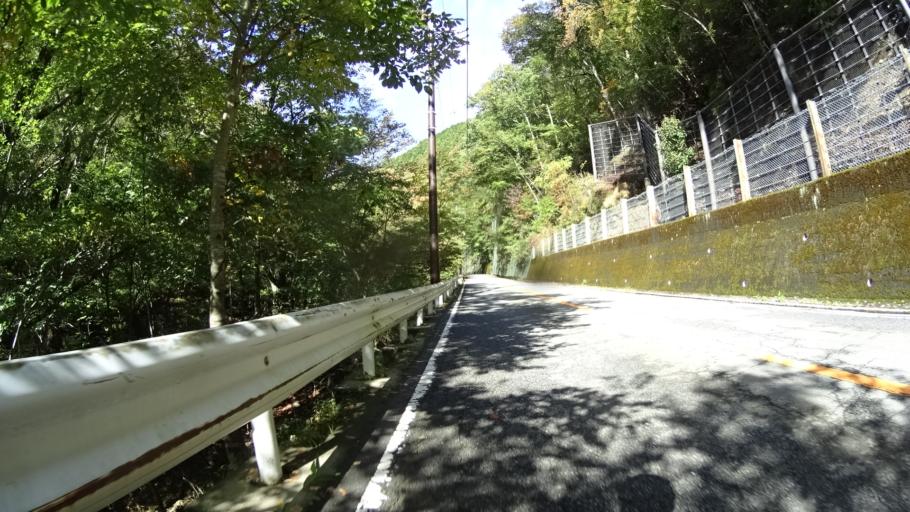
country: JP
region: Yamanashi
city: Enzan
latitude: 35.8053
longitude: 138.8416
